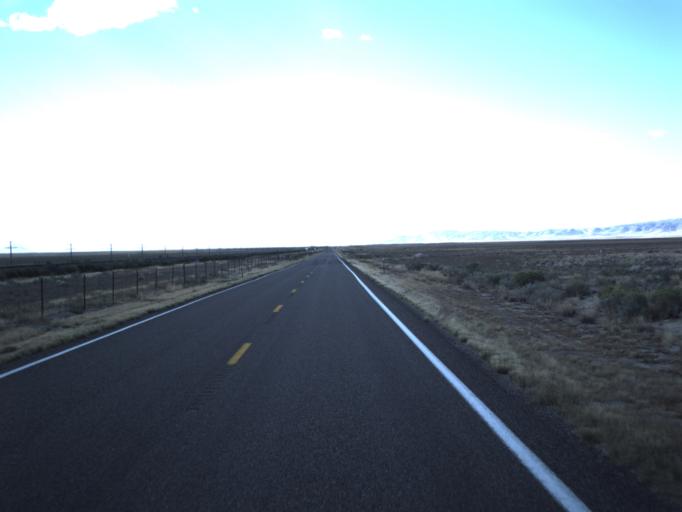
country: US
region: Utah
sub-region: Millard County
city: Delta
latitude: 39.0114
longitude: -112.7830
